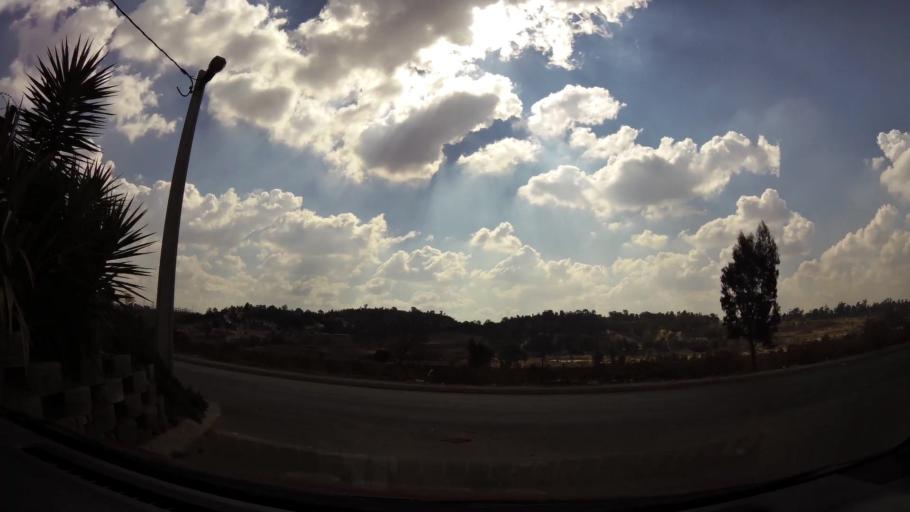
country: ZA
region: Gauteng
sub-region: City of Johannesburg Metropolitan Municipality
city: Roodepoort
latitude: -26.1816
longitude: 27.8554
